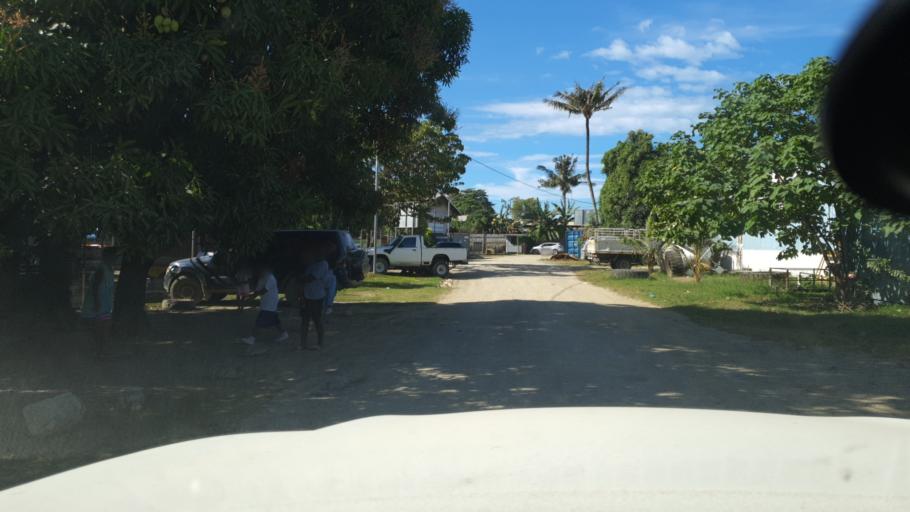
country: SB
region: Guadalcanal
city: Honiara
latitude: -9.4277
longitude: 160.0023
